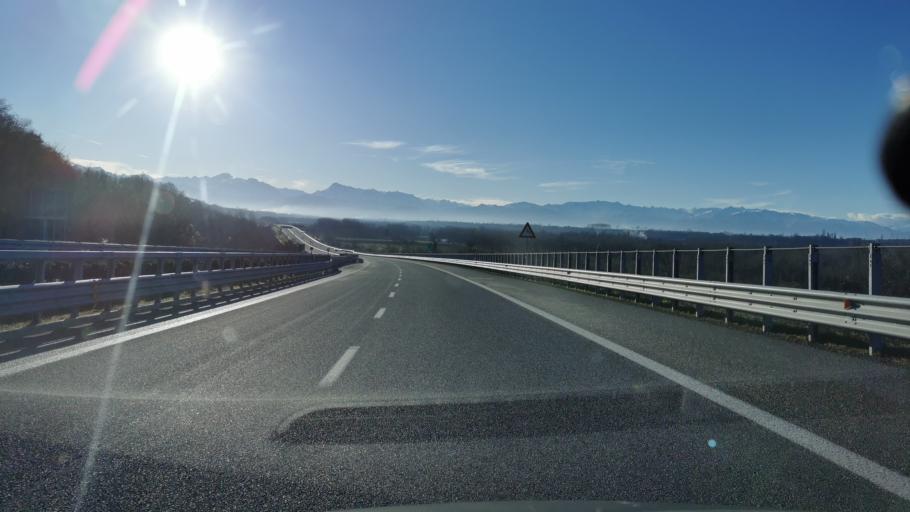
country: IT
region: Piedmont
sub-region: Provincia di Cuneo
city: Montanera
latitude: 44.4755
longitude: 7.6790
